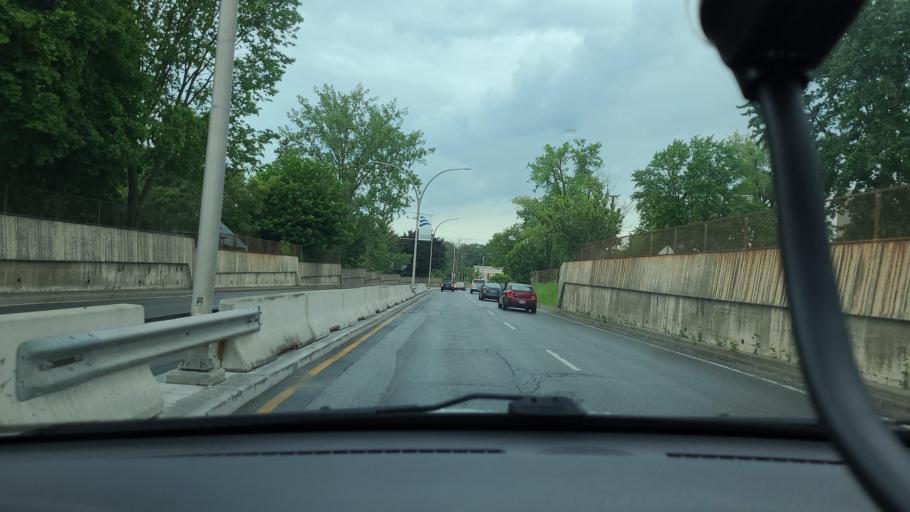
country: CA
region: Quebec
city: Sainte-Anne-de-Bellevue
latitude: 45.4095
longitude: -73.9509
